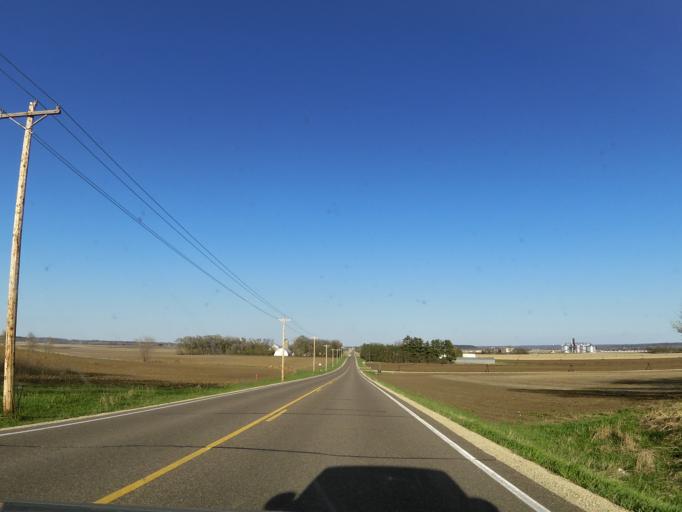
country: US
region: Minnesota
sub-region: Goodhue County
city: Cannon Falls
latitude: 44.5435
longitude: -93.0375
